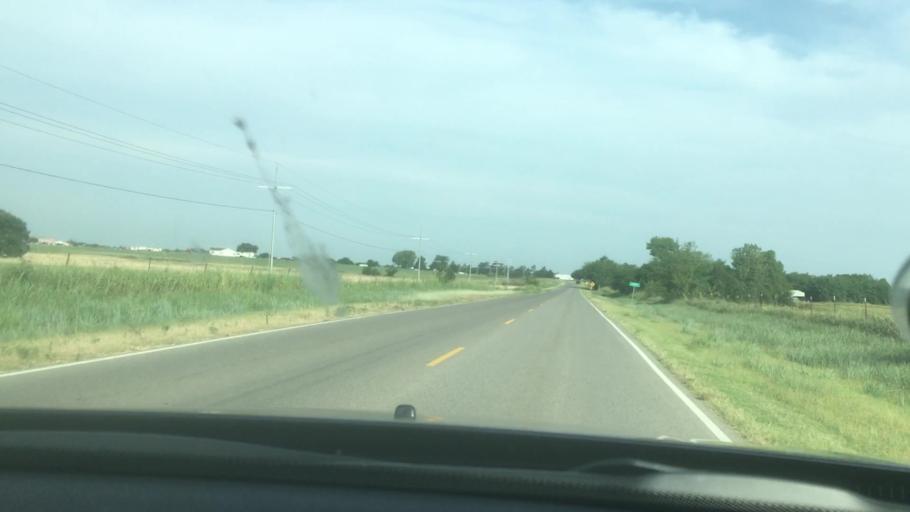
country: US
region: Oklahoma
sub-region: Pontotoc County
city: Ada
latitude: 34.7940
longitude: -96.8111
